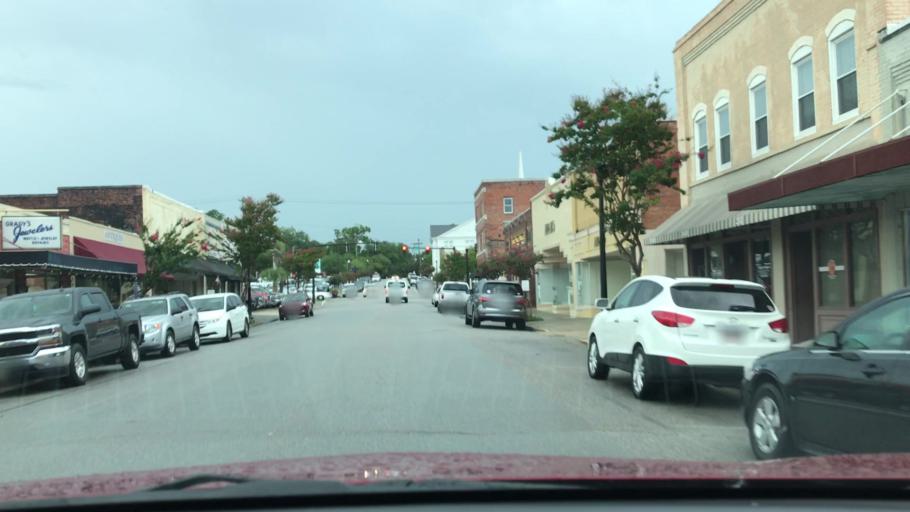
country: US
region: South Carolina
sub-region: Horry County
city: Conway
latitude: 33.8351
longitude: -79.0474
